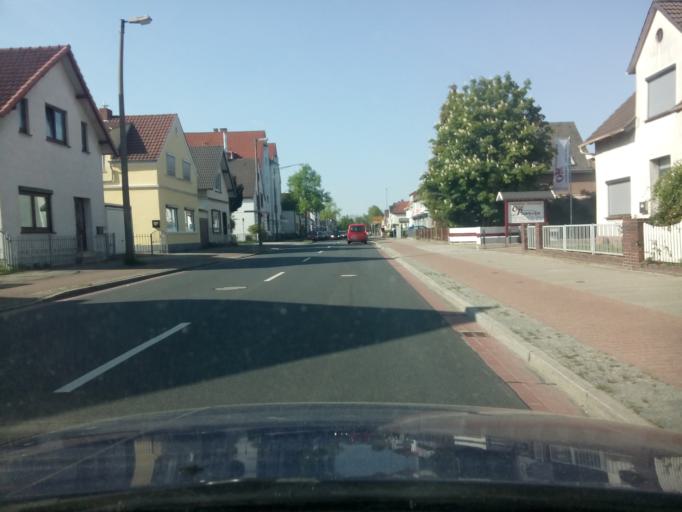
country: DE
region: Lower Saxony
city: Lemwerder
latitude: 53.1809
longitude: 8.6192
